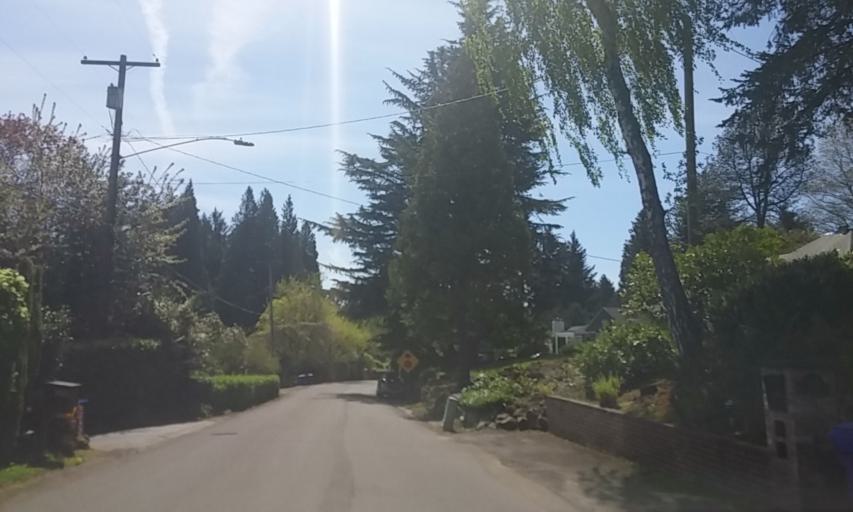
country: US
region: Oregon
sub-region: Washington County
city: West Slope
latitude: 45.5008
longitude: -122.7480
